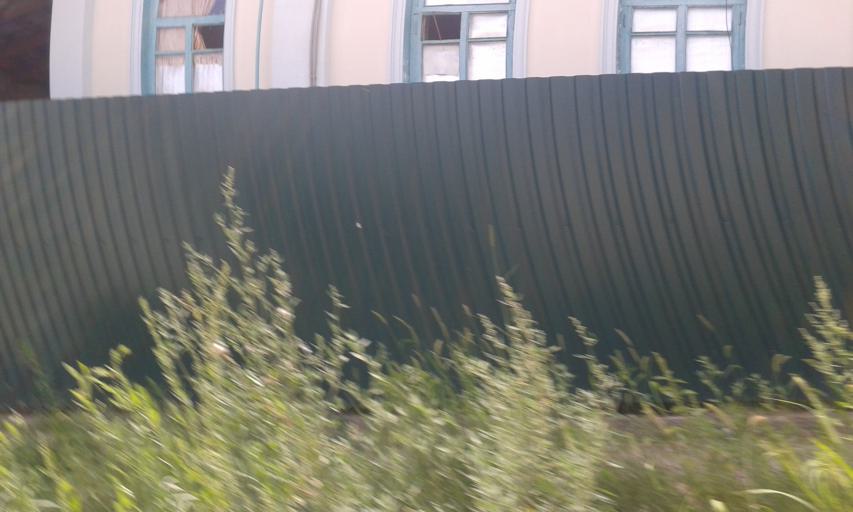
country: RU
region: Volgograd
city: Volgograd
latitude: 48.7592
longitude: 44.4846
